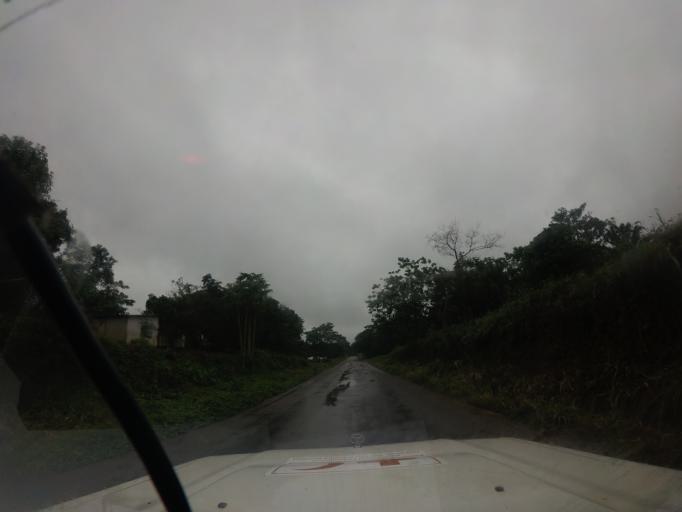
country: SL
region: Northern Province
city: Kabala
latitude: 9.5427
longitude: -11.5750
